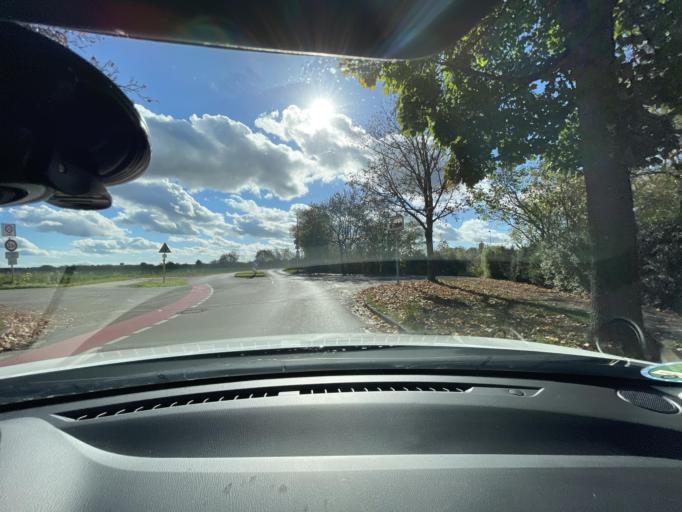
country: DE
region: Bavaria
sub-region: Upper Bavaria
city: Maisach
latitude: 48.2114
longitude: 11.2579
